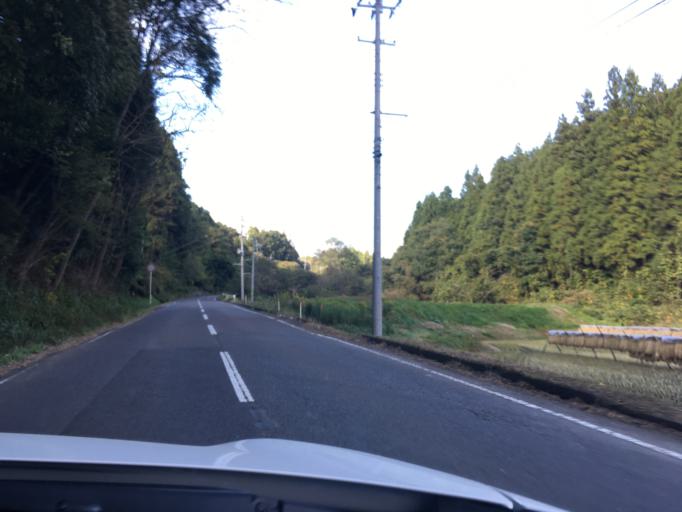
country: JP
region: Fukushima
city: Ishikawa
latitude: 37.1952
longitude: 140.4587
